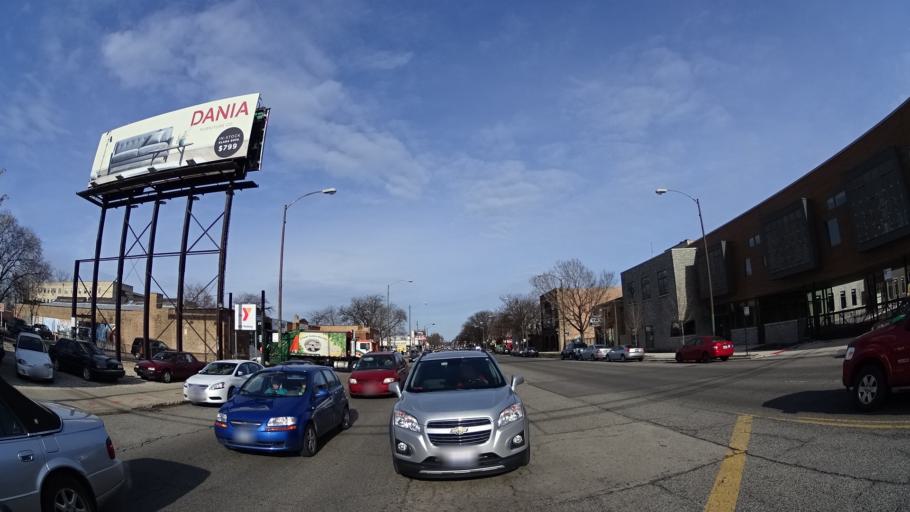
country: US
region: Illinois
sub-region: Cook County
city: Evanston
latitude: 42.0129
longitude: -87.6903
